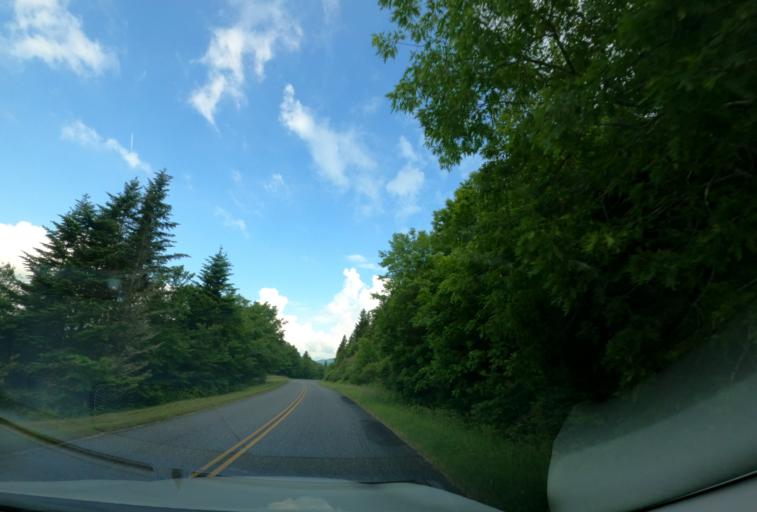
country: US
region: North Carolina
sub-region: Haywood County
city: Hazelwood
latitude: 35.3746
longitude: -83.0034
